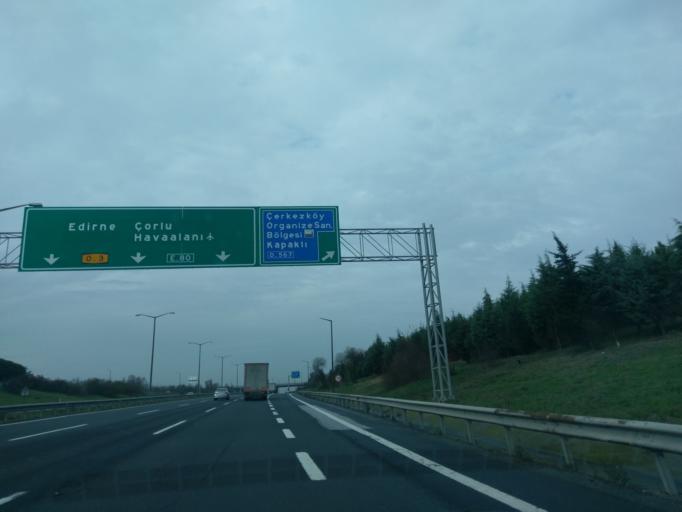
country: TR
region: Istanbul
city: Buyukcavuslu
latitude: 41.1914
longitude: 28.0893
